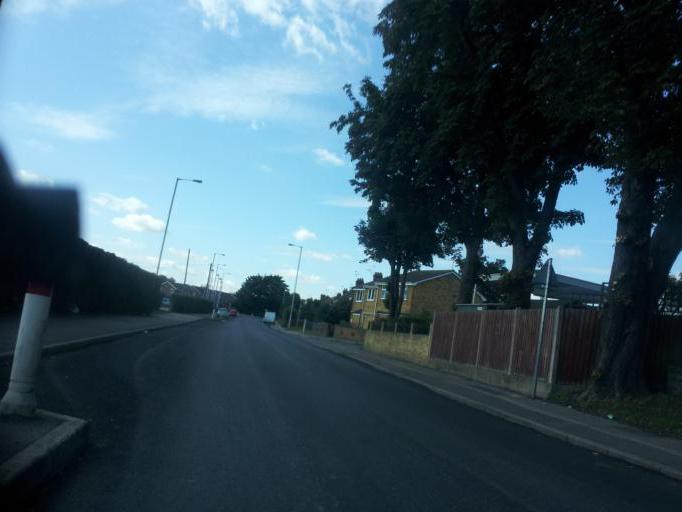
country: GB
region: England
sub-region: Kent
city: Sittingbourne
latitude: 51.3518
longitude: 0.7300
